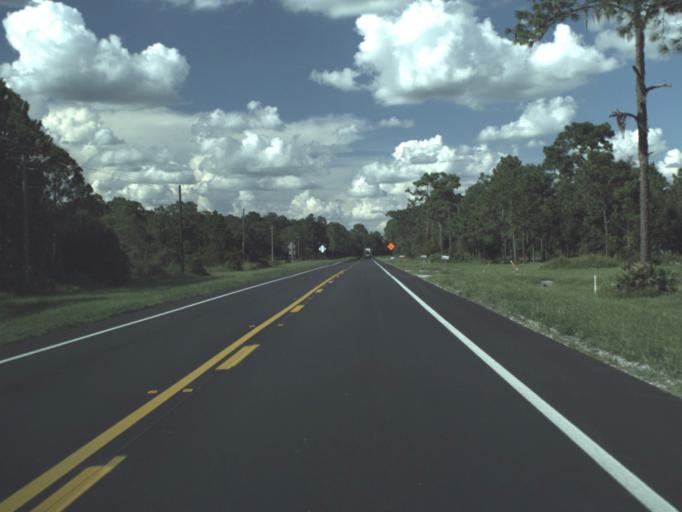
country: US
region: Florida
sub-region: Polk County
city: Polk City
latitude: 28.3276
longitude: -81.8337
